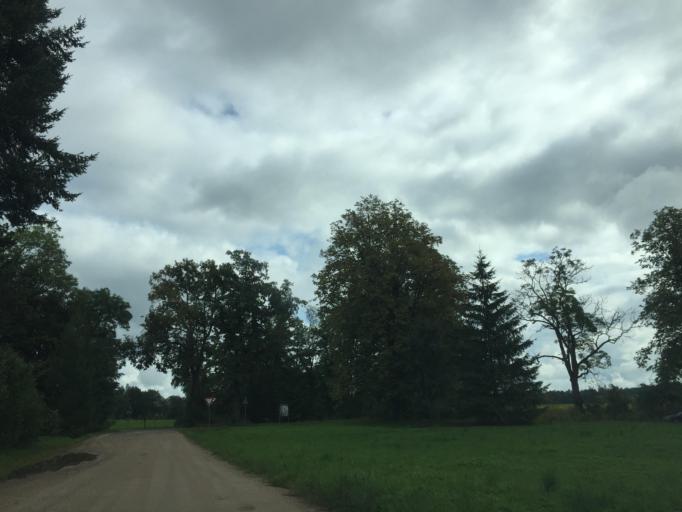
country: LV
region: Cesu Rajons
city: Cesis
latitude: 57.2949
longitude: 25.2331
